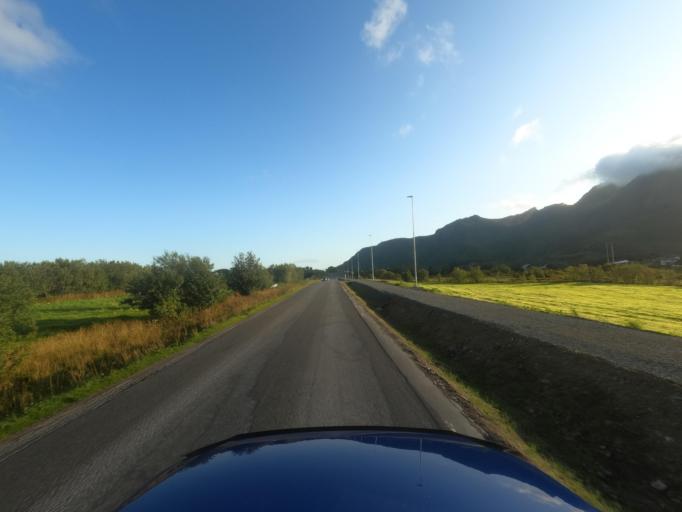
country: NO
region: Nordland
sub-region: Vestvagoy
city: Gravdal
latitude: 68.0931
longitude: 13.5444
